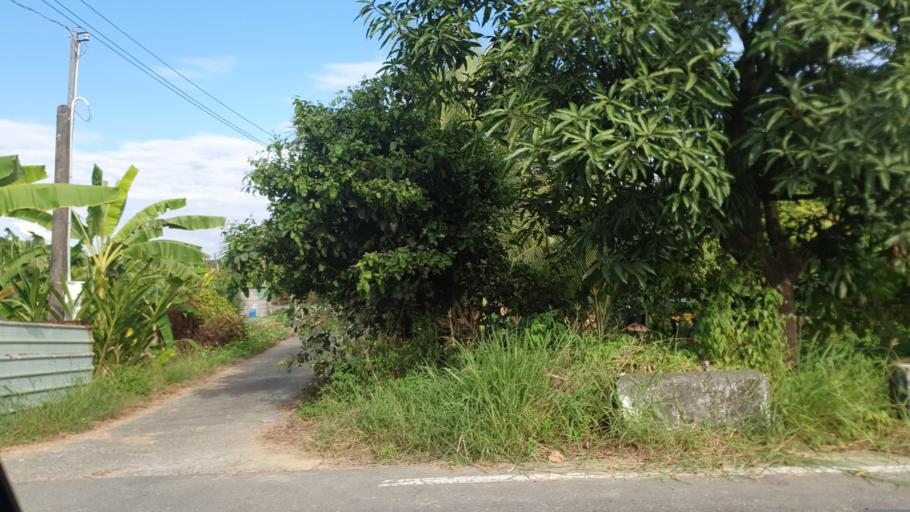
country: TW
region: Taiwan
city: Yujing
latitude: 23.0429
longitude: 120.4230
